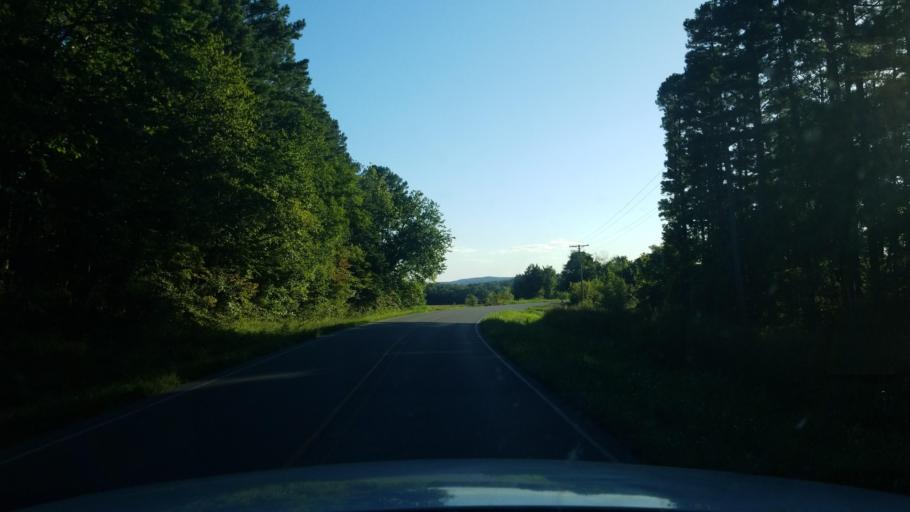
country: US
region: Illinois
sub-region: Hardin County
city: Elizabethtown
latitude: 37.5749
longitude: -88.3893
